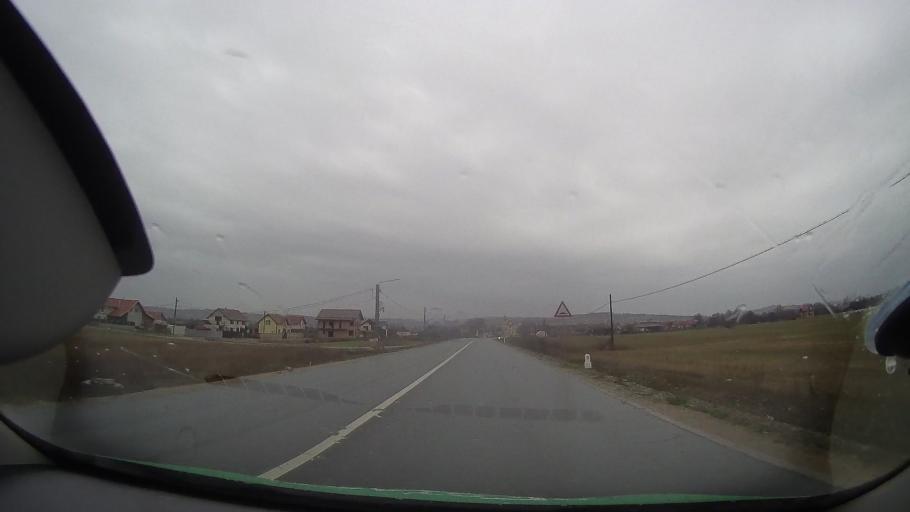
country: RO
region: Bihor
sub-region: Comuna Pocola
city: Pocola
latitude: 46.6912
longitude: 22.2975
